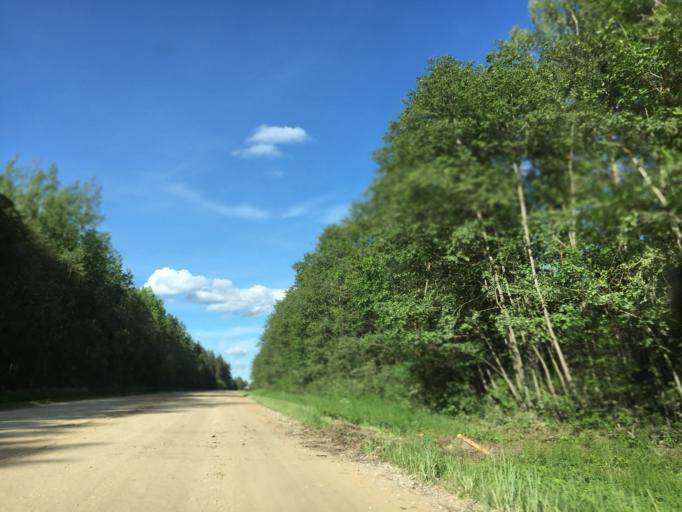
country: LV
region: Vecumnieki
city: Vecumnieki
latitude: 56.4456
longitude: 24.5800
